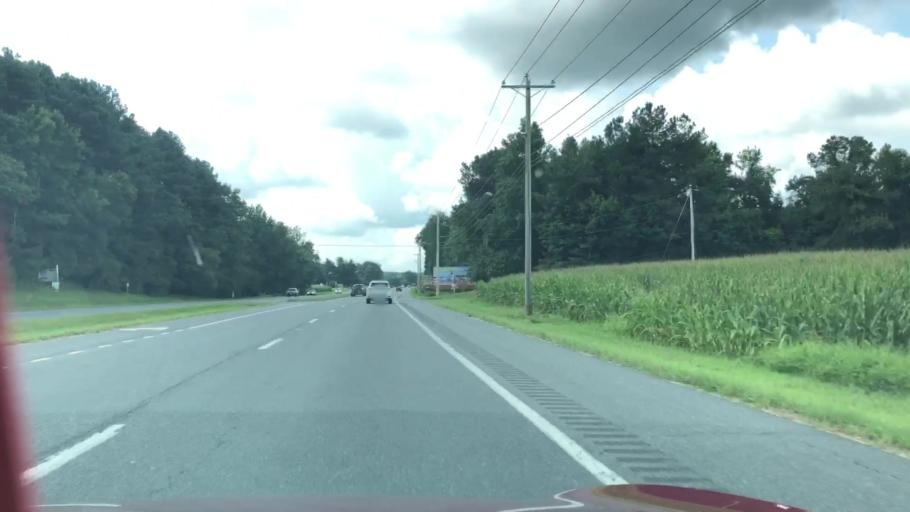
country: US
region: Virginia
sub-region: Accomack County
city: Wattsville
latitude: 37.9647
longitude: -75.5328
